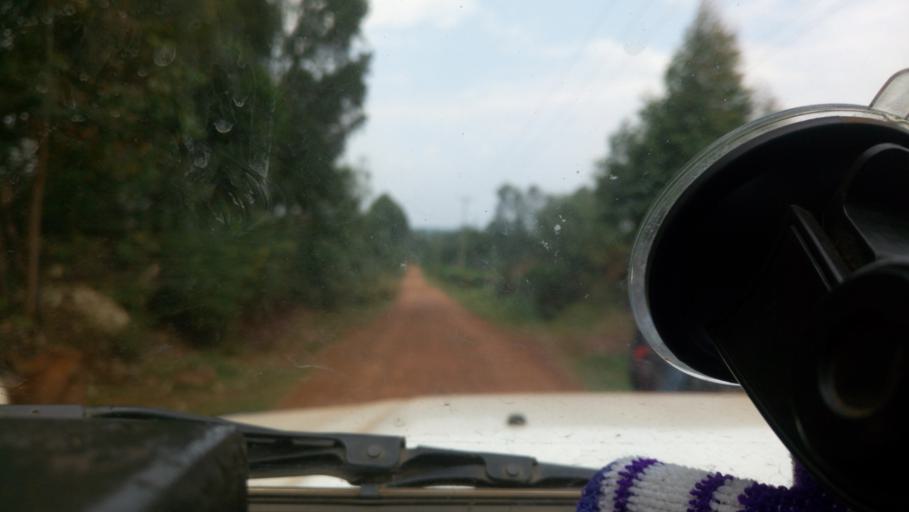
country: KE
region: Kericho
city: Litein
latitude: -0.6383
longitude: 35.1789
